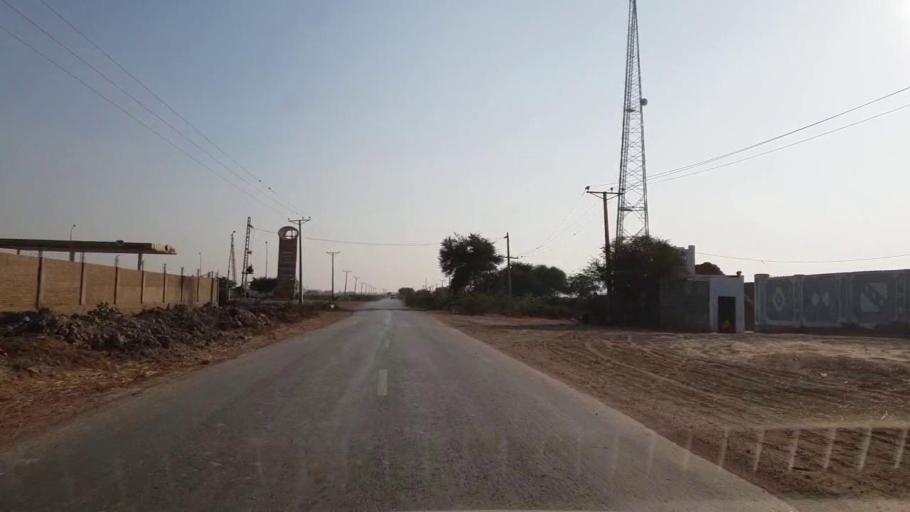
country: PK
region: Sindh
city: Bulri
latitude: 24.8292
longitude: 68.3228
